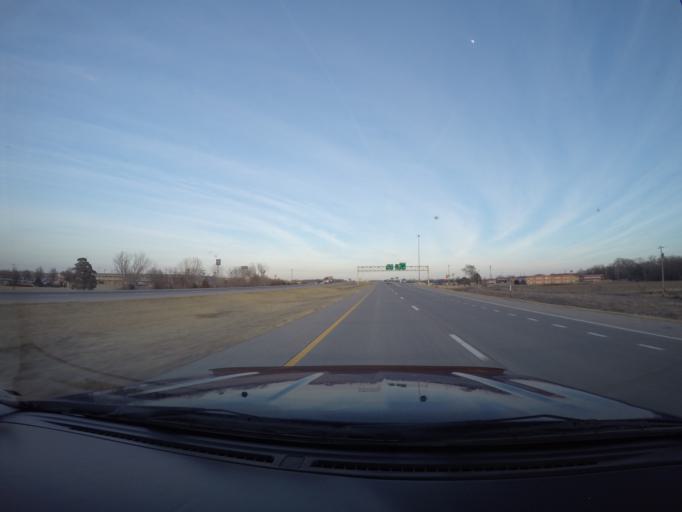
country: US
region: Kansas
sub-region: Saline County
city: Salina
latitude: 38.8760
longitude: -97.6179
